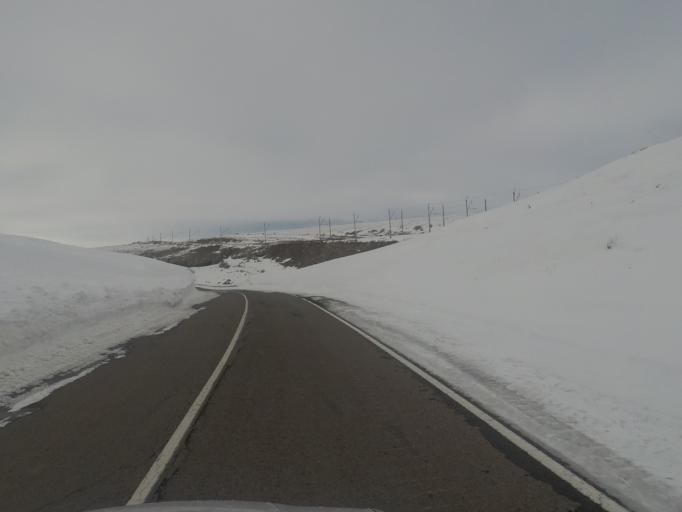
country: GE
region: Kvemo Kartli
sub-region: Tsalka
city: Tsalka
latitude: 41.4414
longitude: 43.8487
